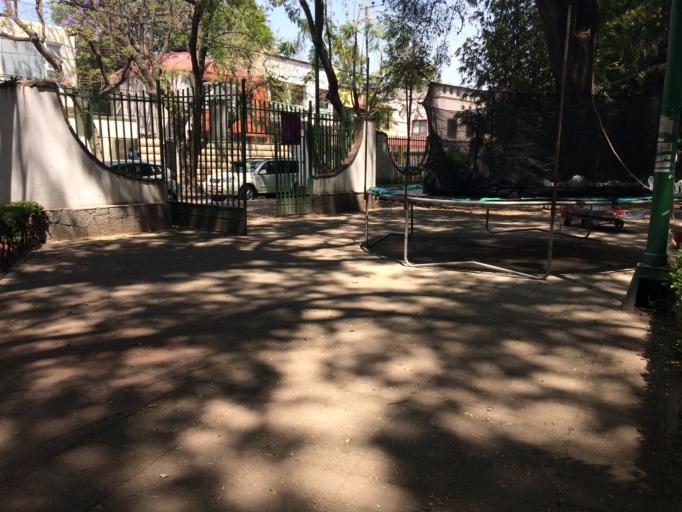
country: MX
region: Mexico City
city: Coyoacan
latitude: 19.3563
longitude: -99.1514
